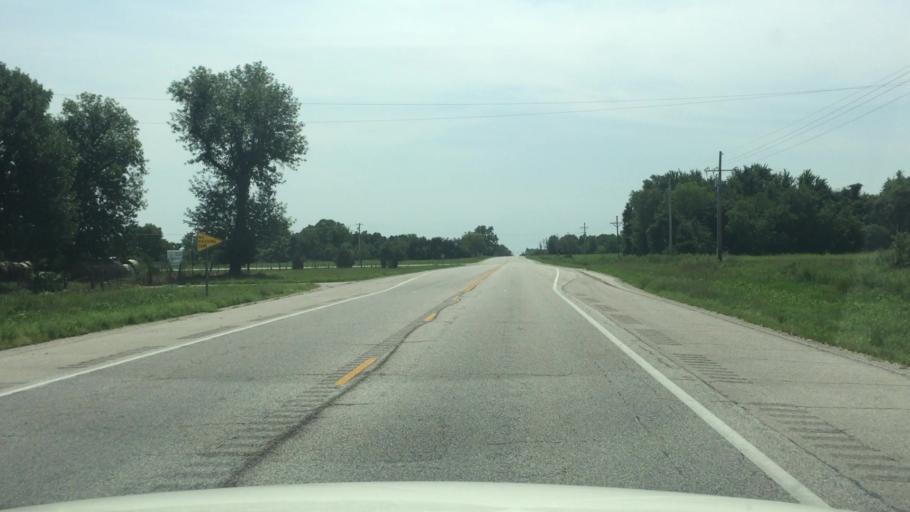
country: US
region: Kansas
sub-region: Cherokee County
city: Galena
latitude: 37.1233
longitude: -94.7044
